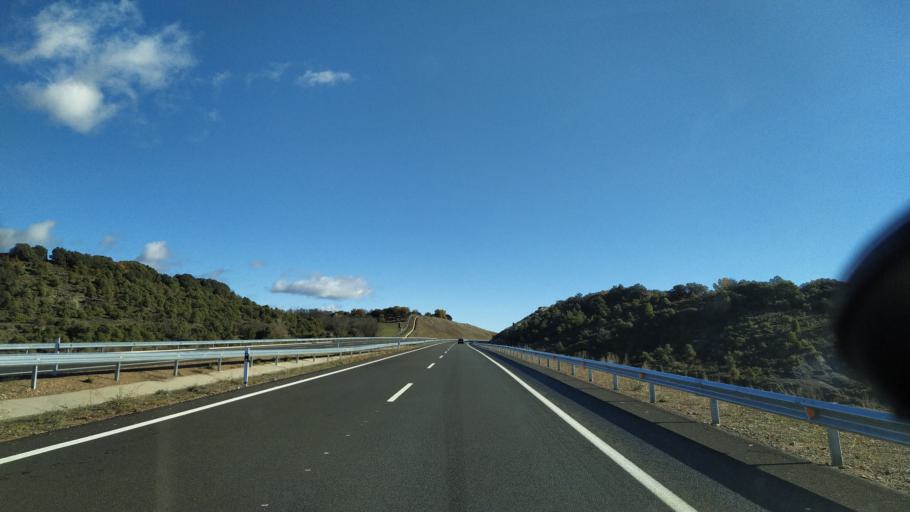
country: ES
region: Aragon
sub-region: Provincia de Huesca
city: Santa Cruz de la Seros
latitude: 42.5634
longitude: -0.6874
